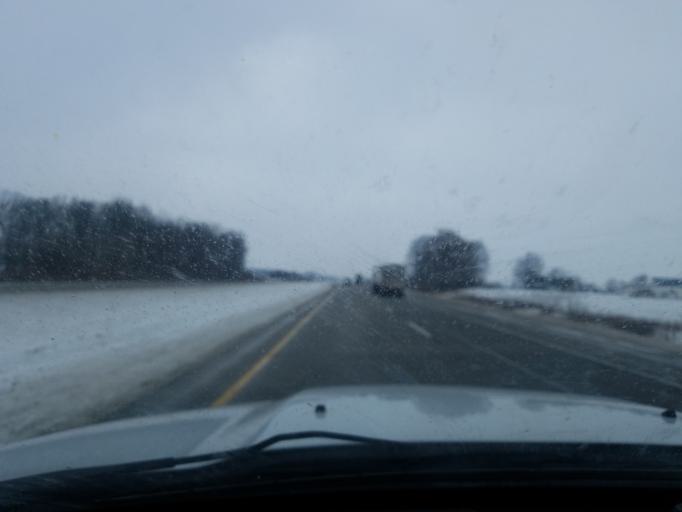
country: US
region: Indiana
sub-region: Marshall County
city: Argos
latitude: 41.1772
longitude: -86.2443
